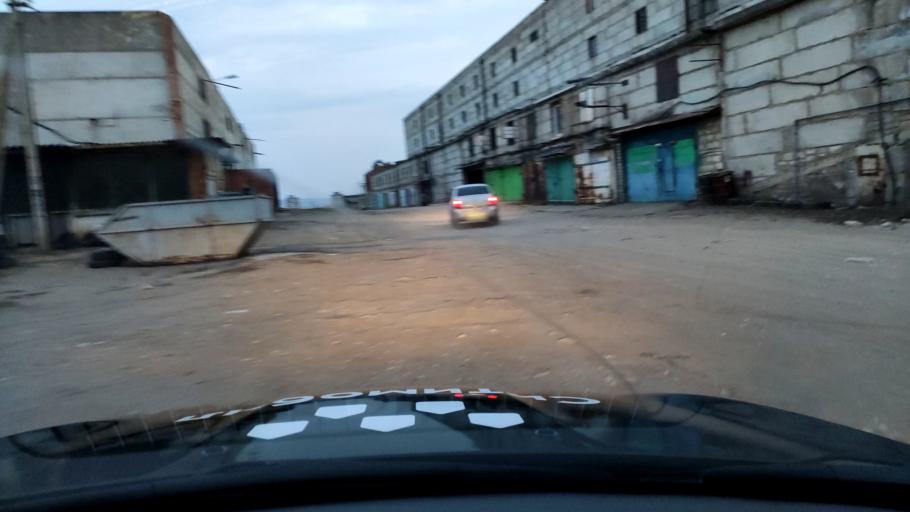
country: RU
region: Samara
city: Zhigulevsk
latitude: 53.4925
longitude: 49.4811
